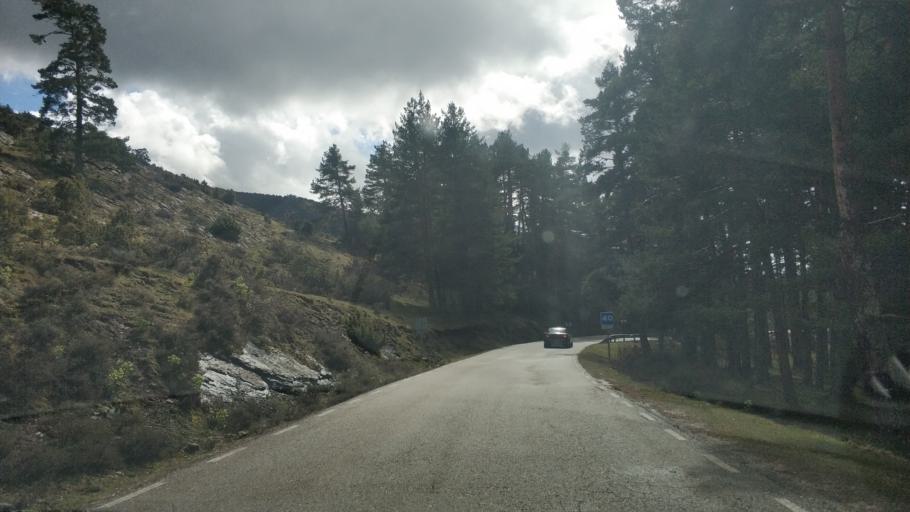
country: ES
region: Castille and Leon
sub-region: Provincia de Burgos
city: Neila
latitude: 42.0392
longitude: -3.0043
